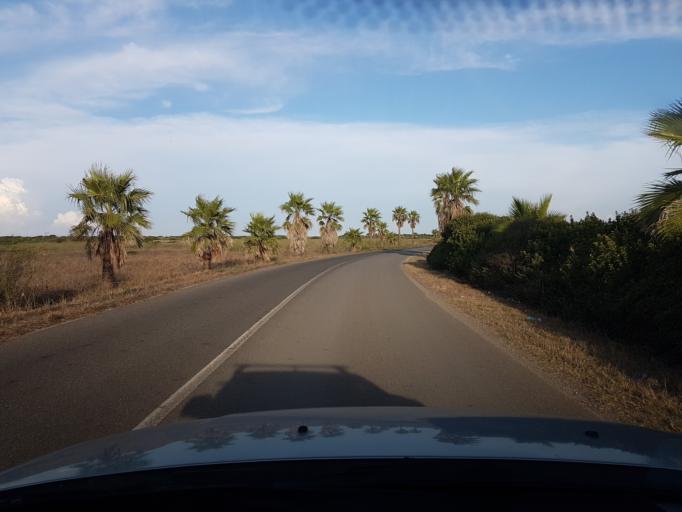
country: IT
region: Sardinia
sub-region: Provincia di Oristano
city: Cabras
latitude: 39.9526
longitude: 8.4075
